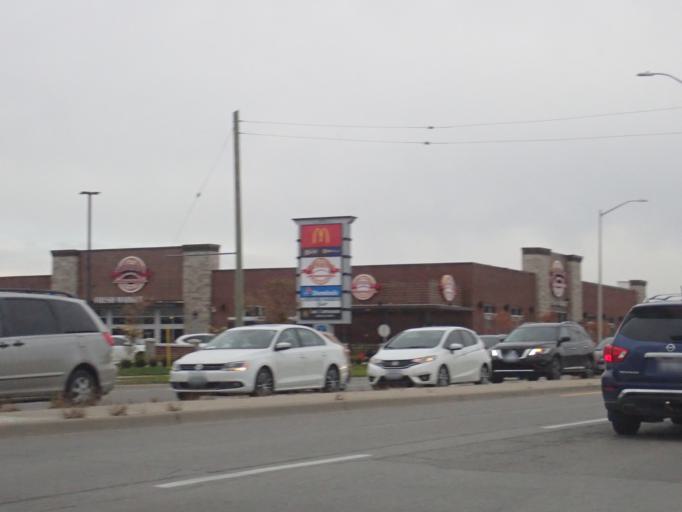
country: CA
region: Ontario
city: London
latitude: 43.0122
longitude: -81.3308
